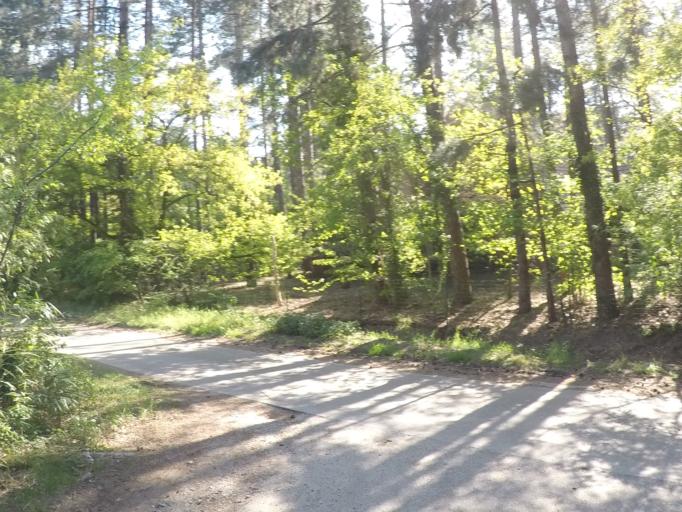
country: BE
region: Flanders
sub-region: Provincie Antwerpen
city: Nijlen
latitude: 51.1708
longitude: 4.7000
